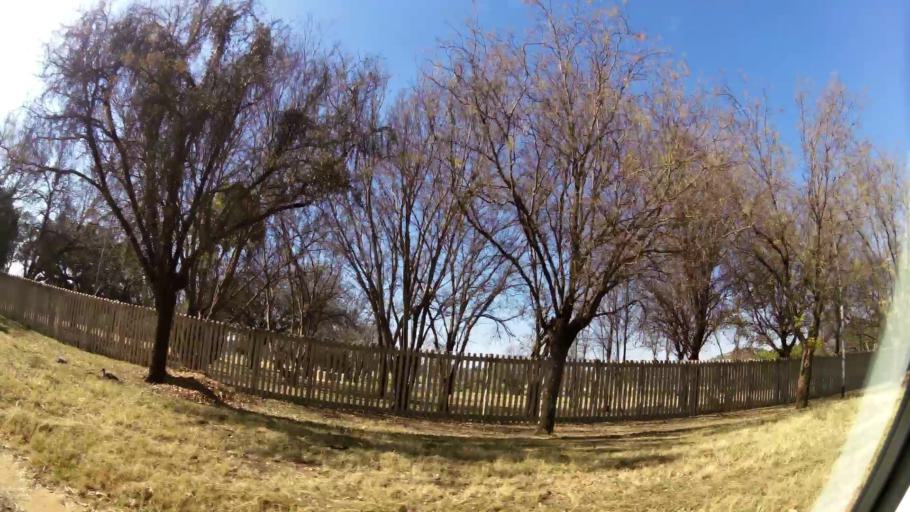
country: ZA
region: Gauteng
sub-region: City of Tshwane Metropolitan Municipality
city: Pretoria
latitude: -25.7457
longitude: 28.2471
